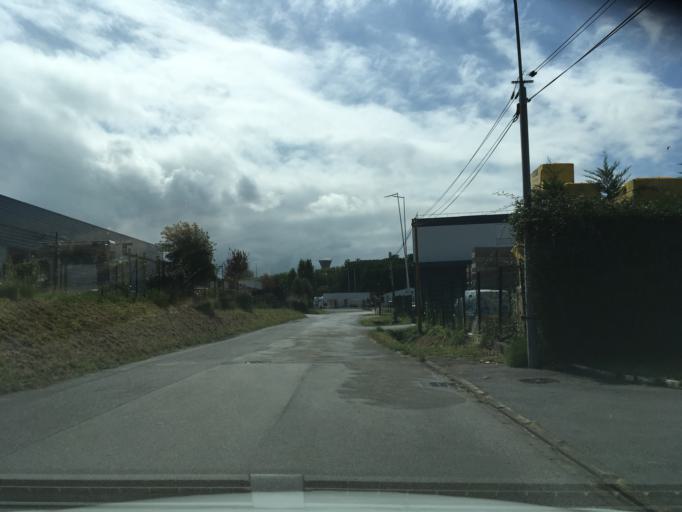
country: FR
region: Aquitaine
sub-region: Departement des Pyrenees-Atlantiques
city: Bayonne
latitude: 43.4912
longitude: -1.4571
